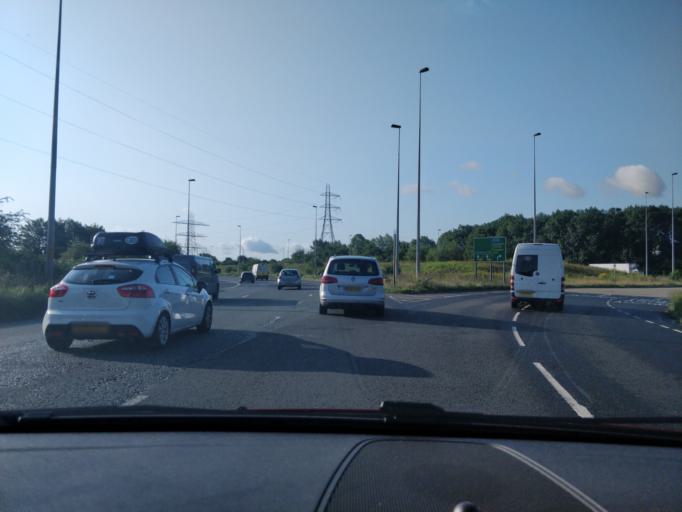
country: GB
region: England
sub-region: Sefton
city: Maghull
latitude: 53.4936
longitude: -2.9509
